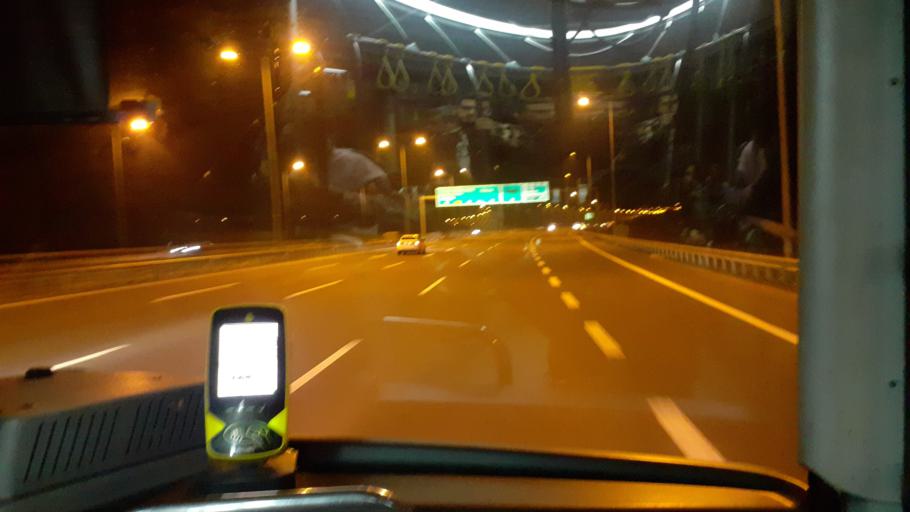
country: TR
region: Istanbul
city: Kemerburgaz
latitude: 41.2374
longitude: 28.8314
